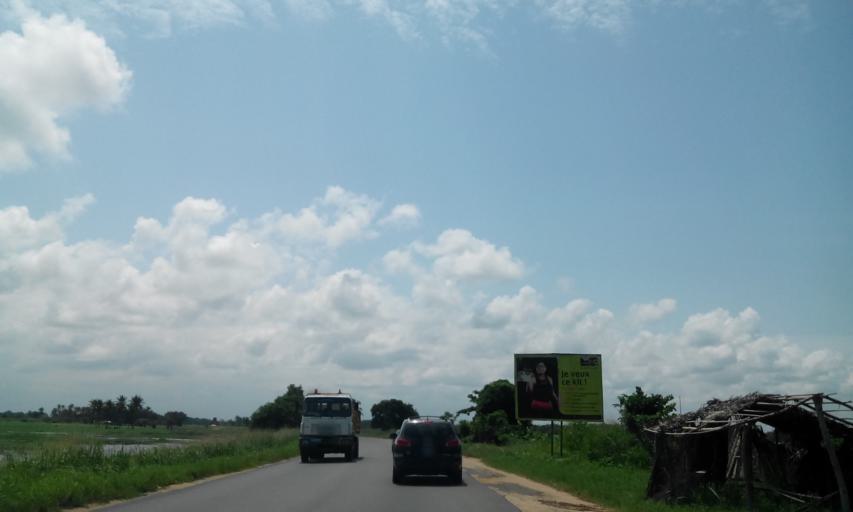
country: CI
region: Sud-Comoe
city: Grand-Bassam
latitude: 5.2149
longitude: -3.7065
